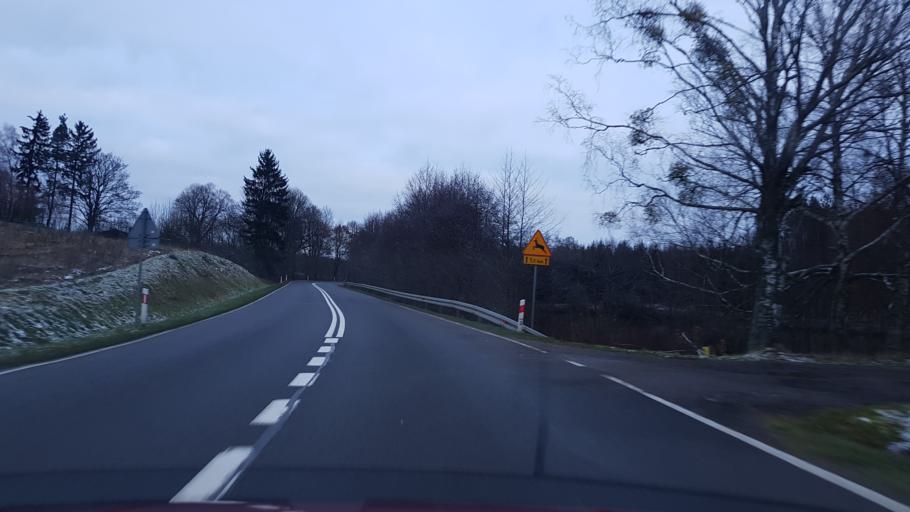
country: PL
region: Pomeranian Voivodeship
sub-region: Powiat bytowski
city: Miastko
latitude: 54.0089
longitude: 17.0817
